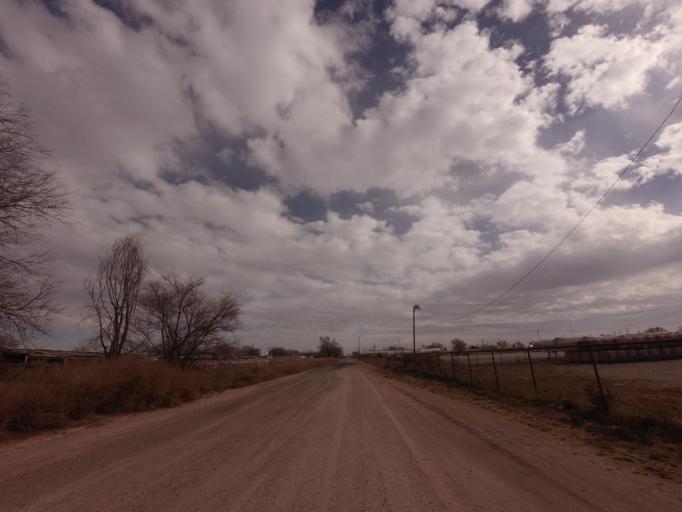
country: US
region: New Mexico
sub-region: Curry County
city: Clovis
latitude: 34.3928
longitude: -103.2198
